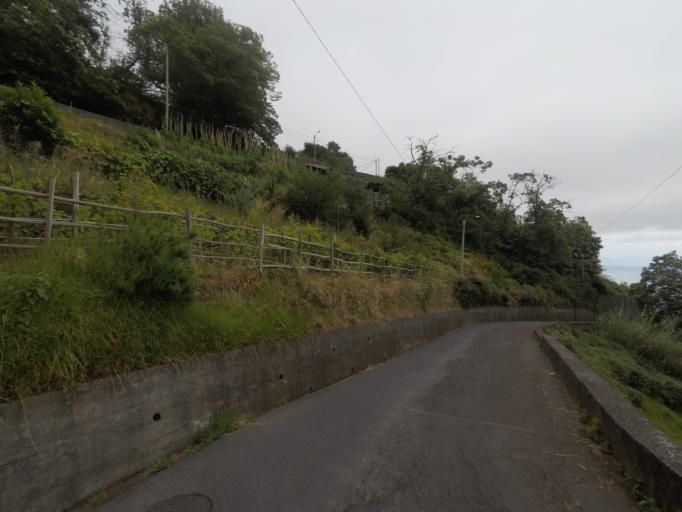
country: PT
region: Madeira
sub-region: Funchal
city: Nossa Senhora do Monte
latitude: 32.6808
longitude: -16.9388
